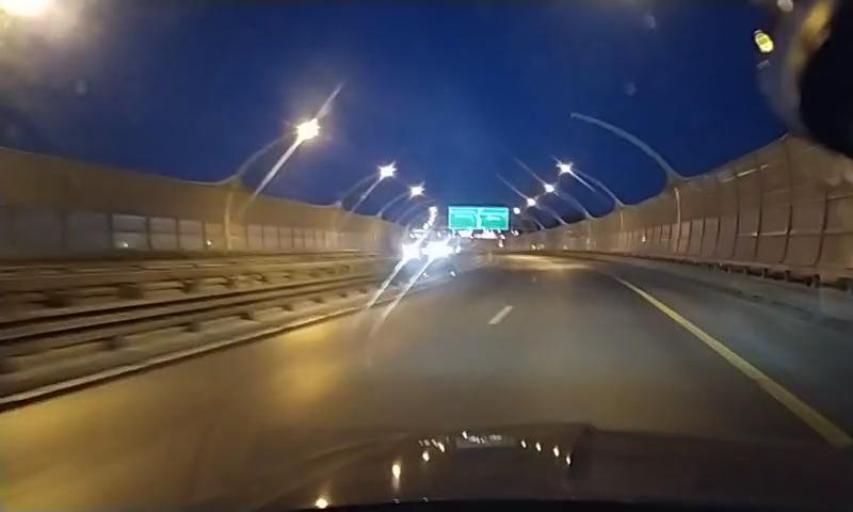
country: RU
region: St.-Petersburg
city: Beloostrov
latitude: 60.1471
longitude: 30.0056
